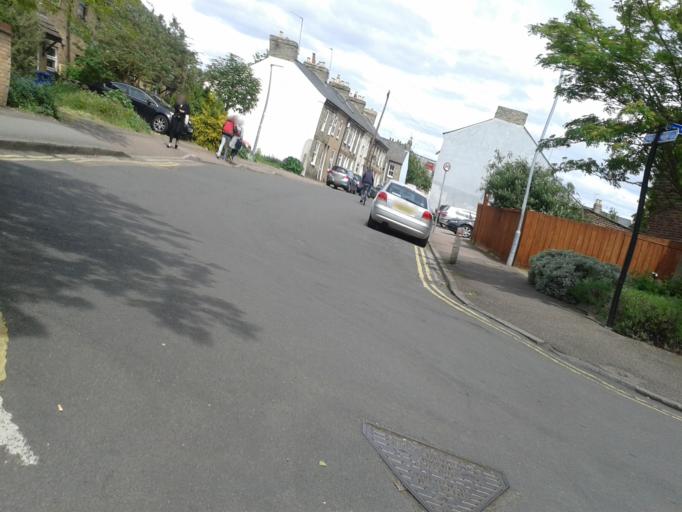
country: GB
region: England
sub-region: Cambridgeshire
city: Cambridge
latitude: 52.1959
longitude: 0.1421
